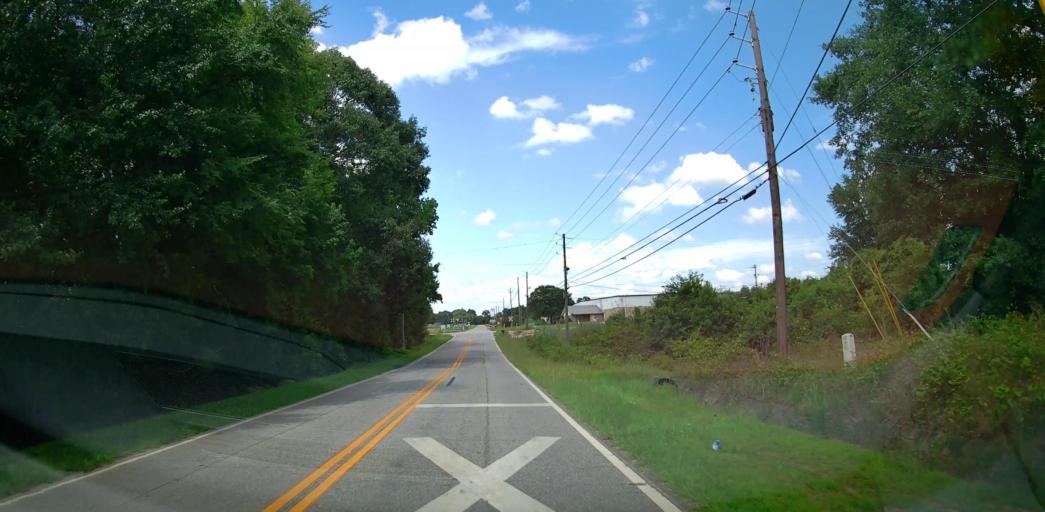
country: US
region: Georgia
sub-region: Houston County
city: Centerville
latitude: 32.6983
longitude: -83.6644
